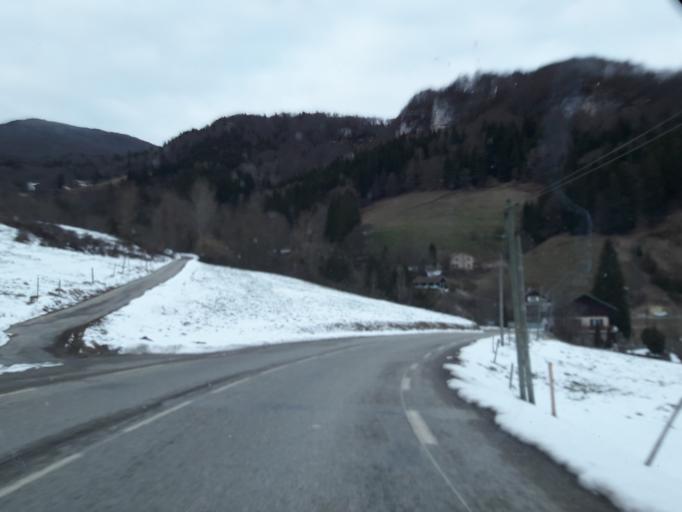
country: FR
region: Rhone-Alpes
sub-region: Departement de la Drome
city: Saint-Laurent-en-Royans
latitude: 44.9992
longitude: 5.4227
